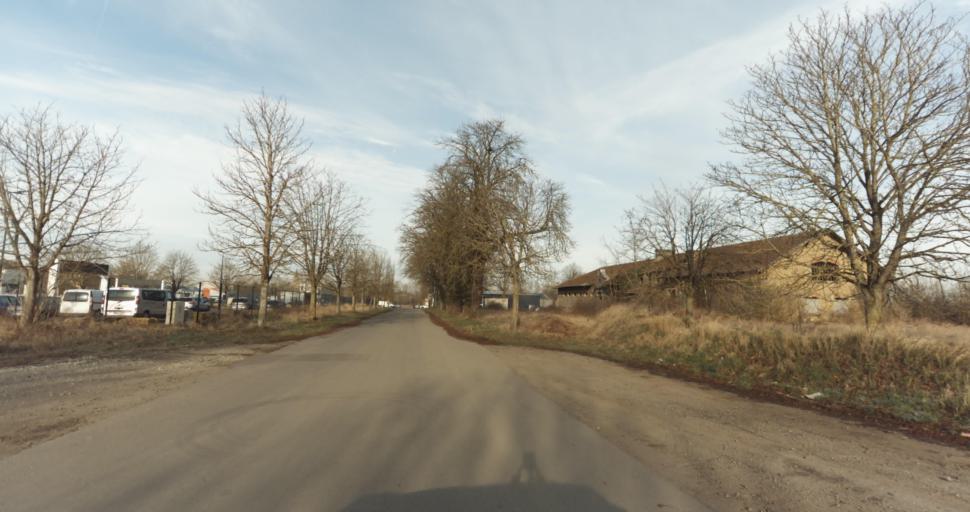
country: FR
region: Lorraine
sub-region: Departement de Meurthe-et-Moselle
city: Jarny
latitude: 49.1550
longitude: 5.8939
